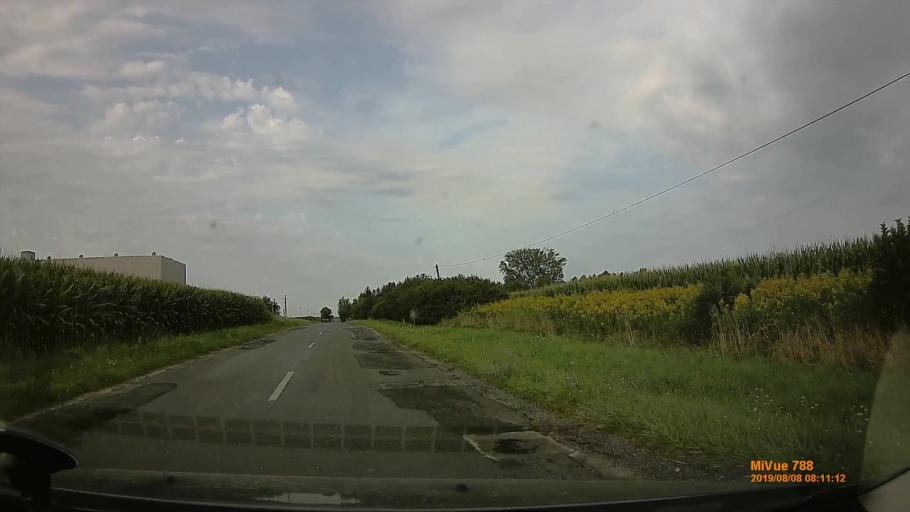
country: HU
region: Zala
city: Murakeresztur
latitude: 46.4249
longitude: 16.8833
